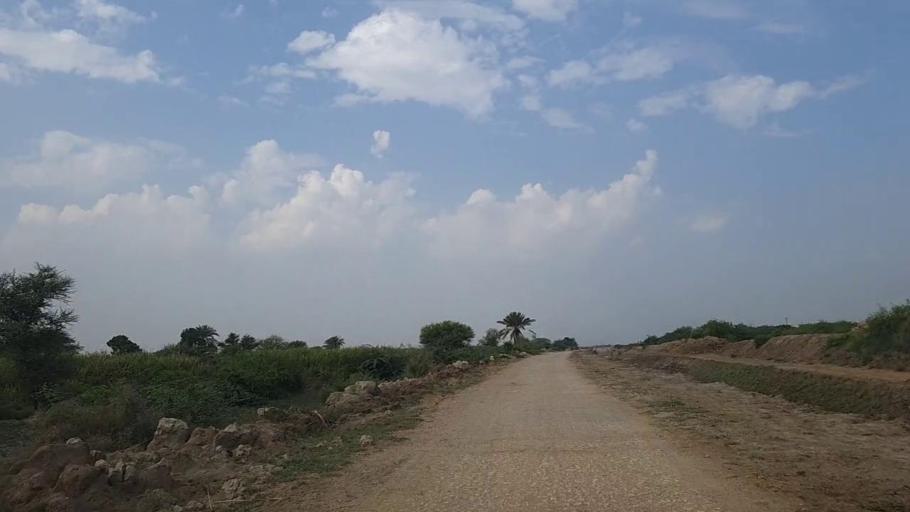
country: PK
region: Sindh
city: Daro Mehar
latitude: 24.7187
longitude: 68.1391
